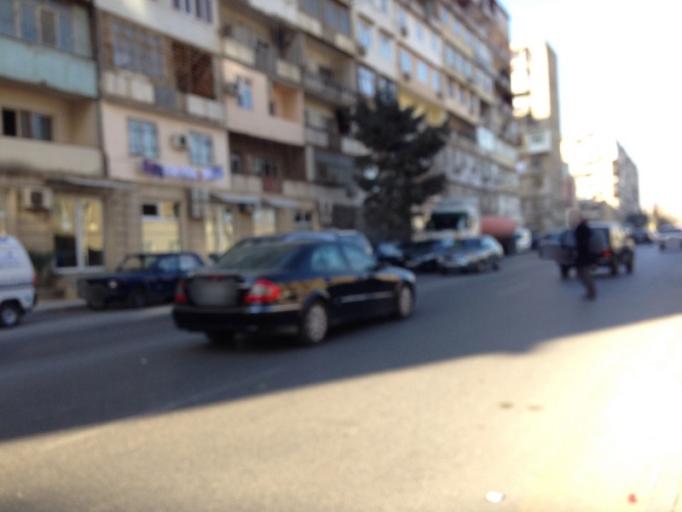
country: AZ
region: Baki
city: Baku
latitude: 40.4071
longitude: 49.8749
